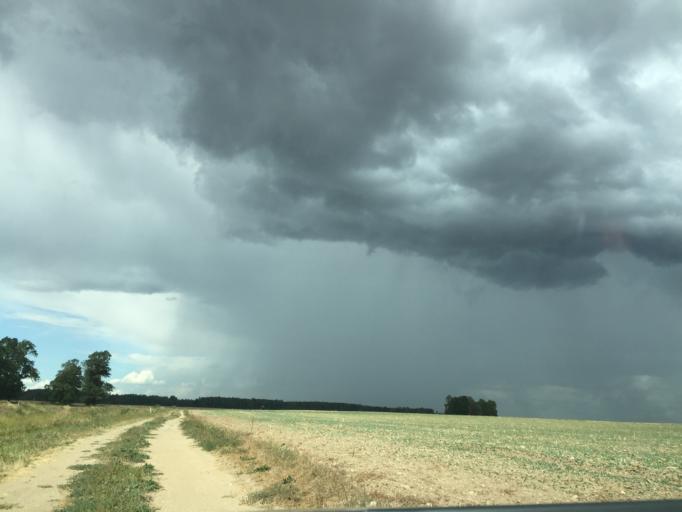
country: LT
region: Siauliu apskritis
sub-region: Joniskis
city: Joniskis
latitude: 56.2888
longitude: 23.7268
